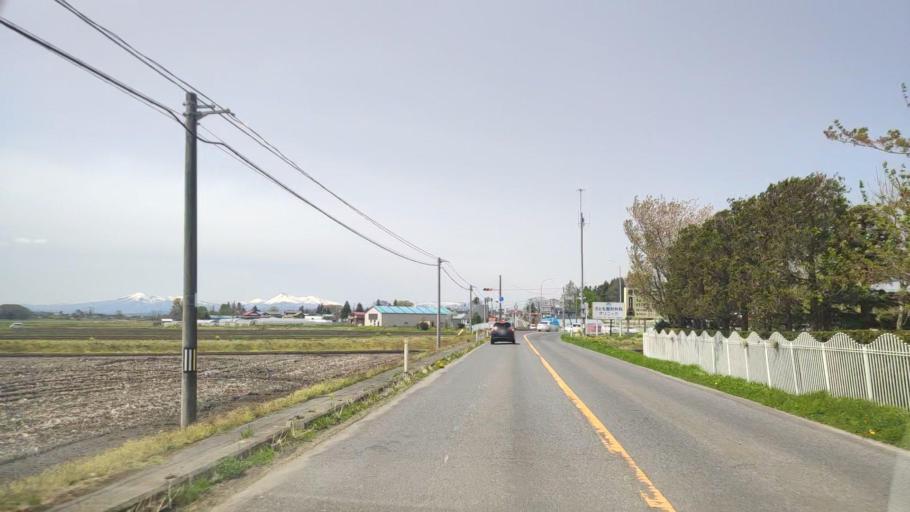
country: JP
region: Aomori
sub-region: Misawa Shi
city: Inuotose
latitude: 40.6046
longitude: 141.2942
